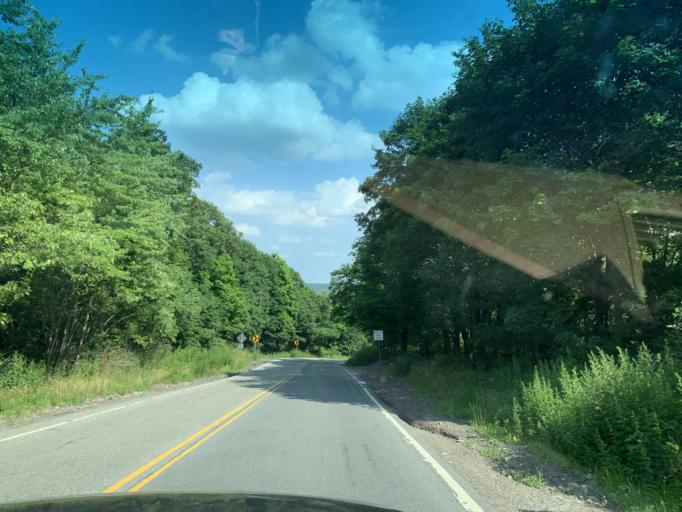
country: US
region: Pennsylvania
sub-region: Schuylkill County
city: Ashland
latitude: 40.7994
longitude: -76.3394
